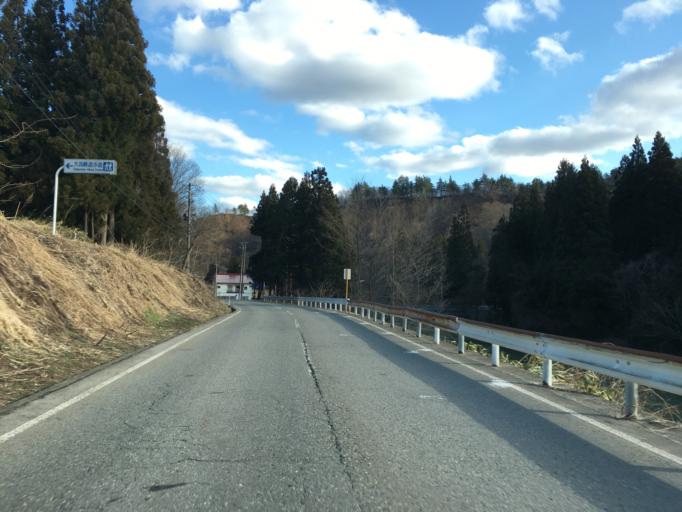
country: JP
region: Yamagata
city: Nagai
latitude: 37.9798
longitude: 139.9388
